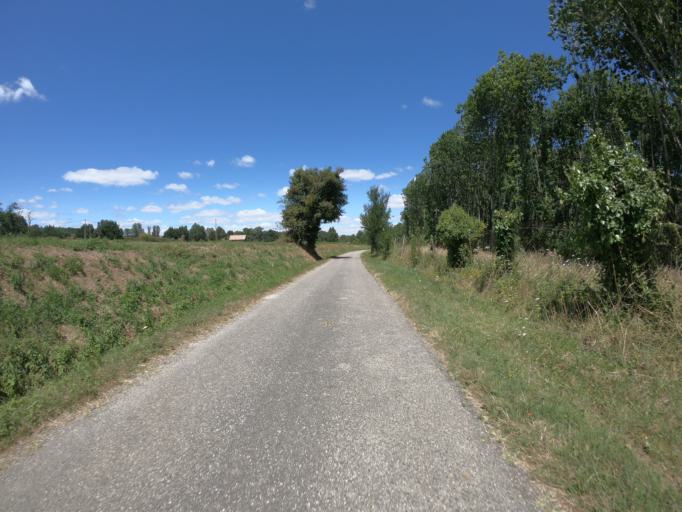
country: FR
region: Midi-Pyrenees
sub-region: Departement de l'Ariege
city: Verniolle
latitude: 43.0803
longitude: 1.7169
